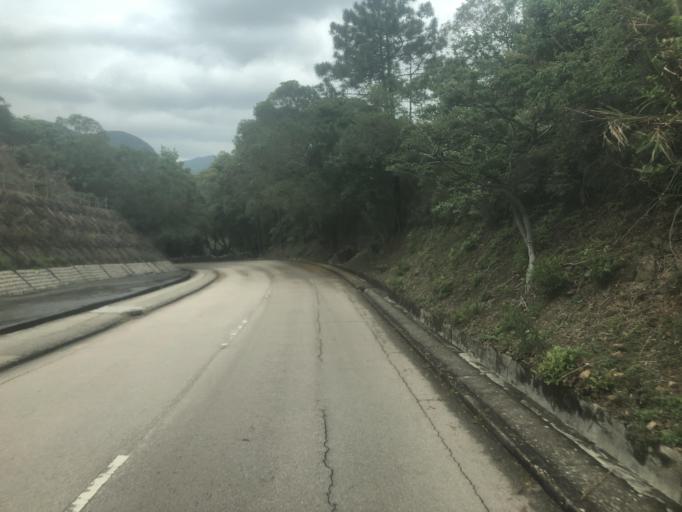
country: HK
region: Sai Kung
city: Sai Kung
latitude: 22.3955
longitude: 114.3295
